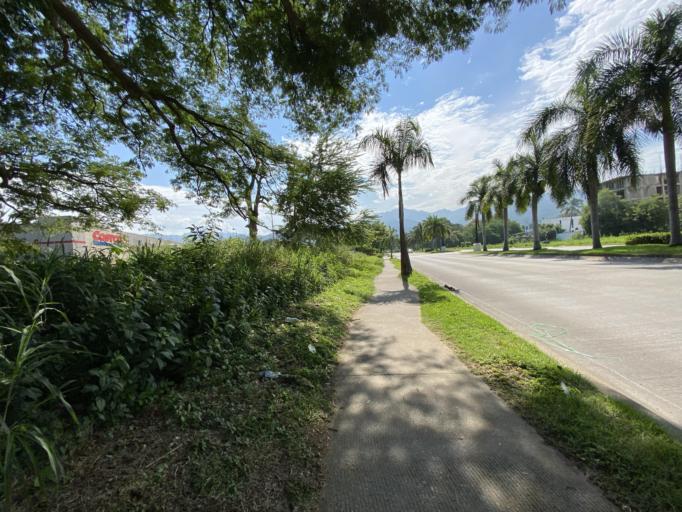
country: MX
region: Jalisco
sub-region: Puerto Vallarta
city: Puerto Vallarta
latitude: 20.6406
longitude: -105.2250
